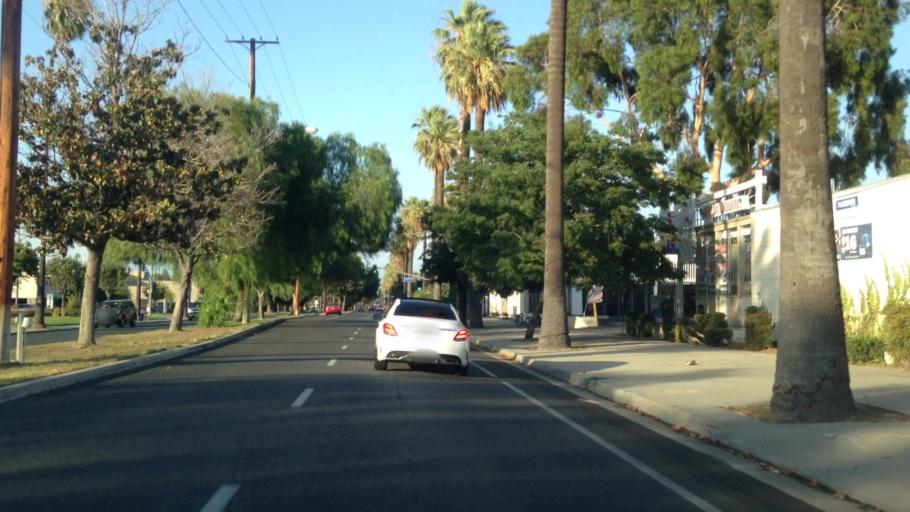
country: US
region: California
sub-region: Riverside County
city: Riverside
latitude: 33.9228
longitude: -117.4421
